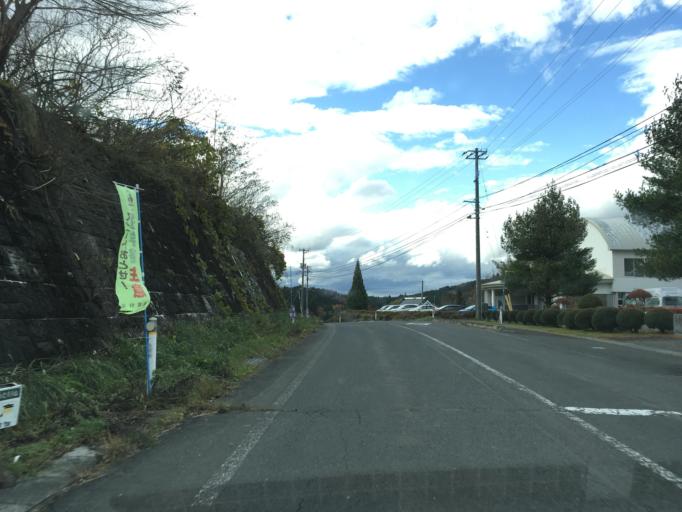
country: JP
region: Iwate
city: Ichinoseki
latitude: 38.8990
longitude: 141.4301
